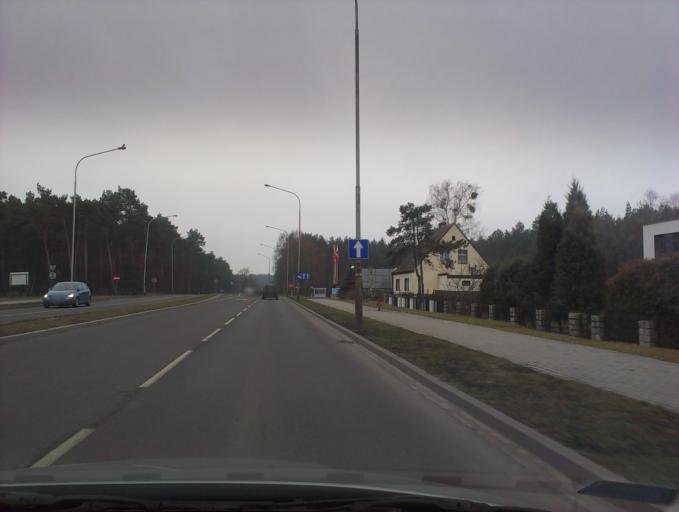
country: PL
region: Greater Poland Voivodeship
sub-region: Powiat pilski
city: Pila
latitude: 53.1269
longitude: 16.7528
